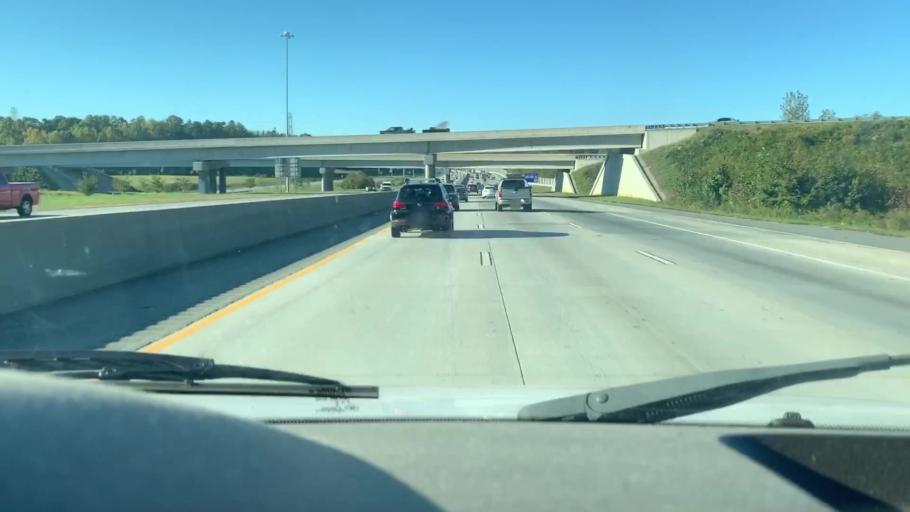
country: US
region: North Carolina
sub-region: Cabarrus County
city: Harrisburg
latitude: 35.3475
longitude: -80.7334
